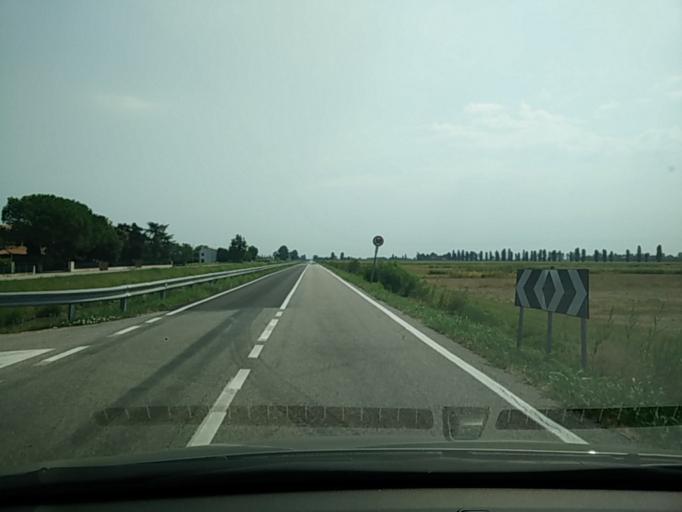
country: IT
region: Veneto
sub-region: Provincia di Venezia
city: Torre di Mosto
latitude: 45.6564
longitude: 12.6740
